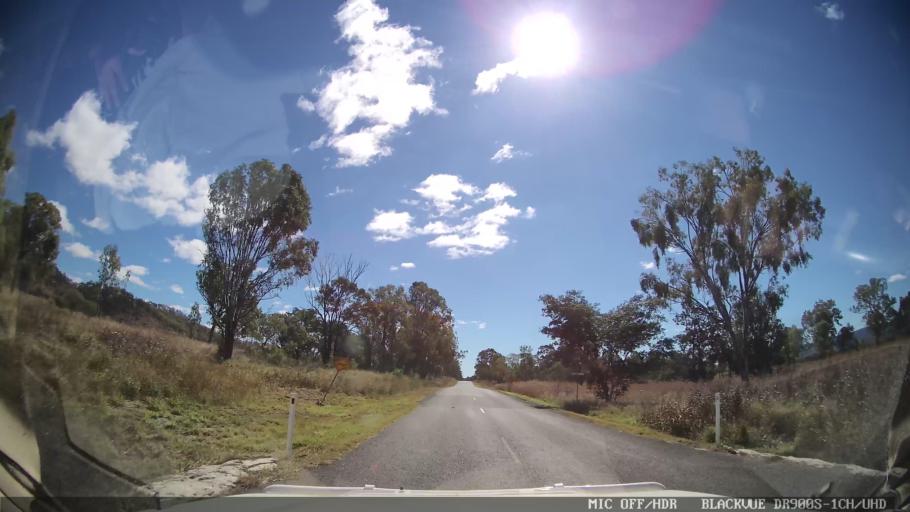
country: AU
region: Queensland
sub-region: Gladstone
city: Toolooa
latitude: -24.4468
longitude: 151.3433
